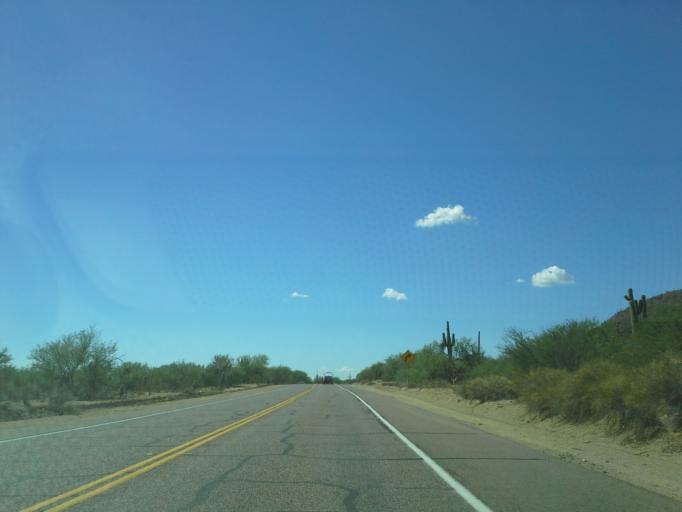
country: US
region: Arizona
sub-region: Pinal County
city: Apache Junction
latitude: 33.5515
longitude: -111.5588
